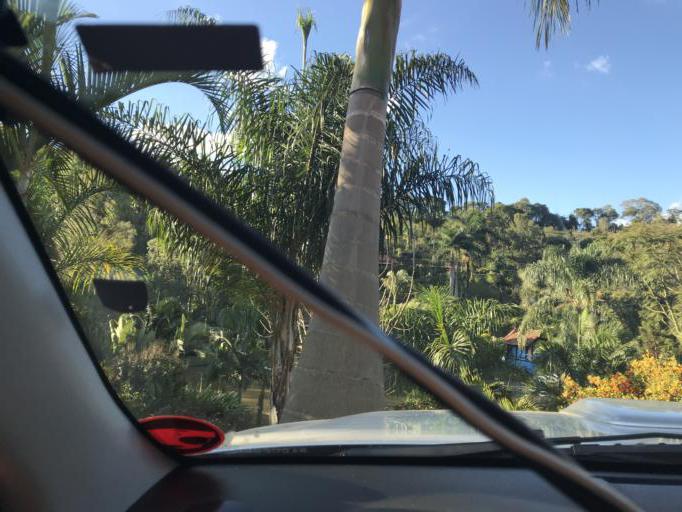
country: BR
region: Minas Gerais
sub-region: Baependi
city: Baependi
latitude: -21.9186
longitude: -44.8533
